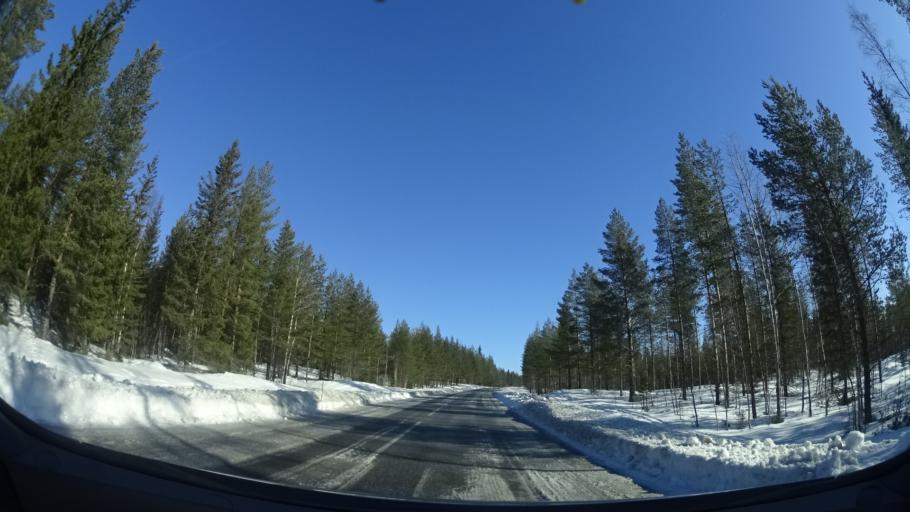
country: SE
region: Vaesterbotten
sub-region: Skelleftea Kommun
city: Langsele
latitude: 65.1232
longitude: 20.1091
